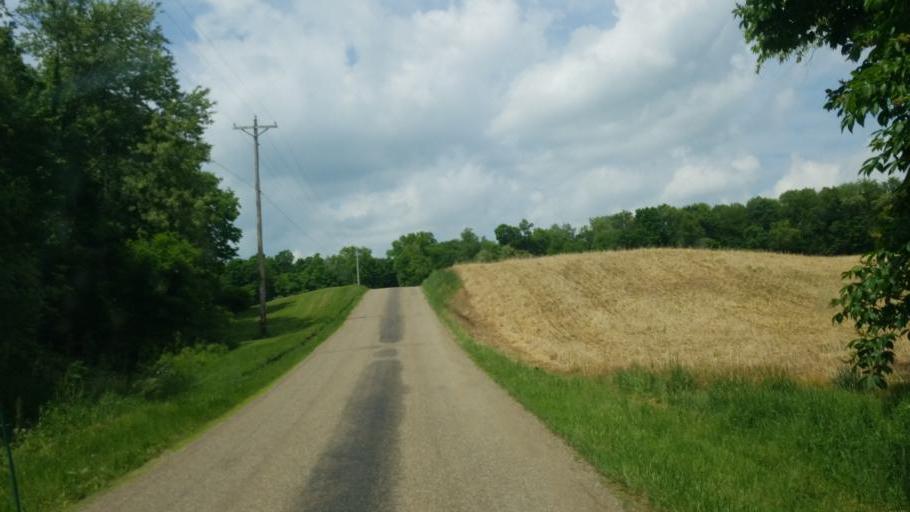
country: US
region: Ohio
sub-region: Ashland County
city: Loudonville
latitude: 40.6551
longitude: -82.3581
